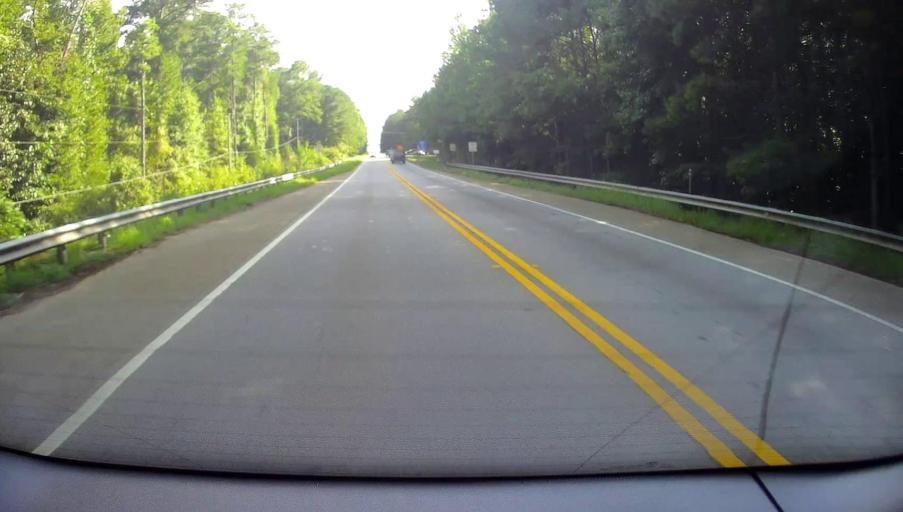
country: US
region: Georgia
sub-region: Coweta County
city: Senoia
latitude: 33.3048
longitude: -84.5345
